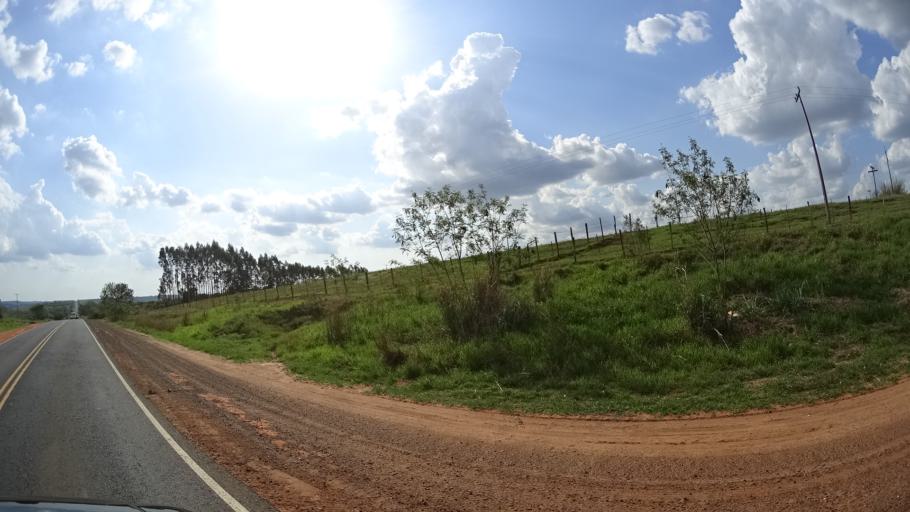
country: BR
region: Sao Paulo
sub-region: Urupes
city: Urupes
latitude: -21.1905
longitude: -49.3040
